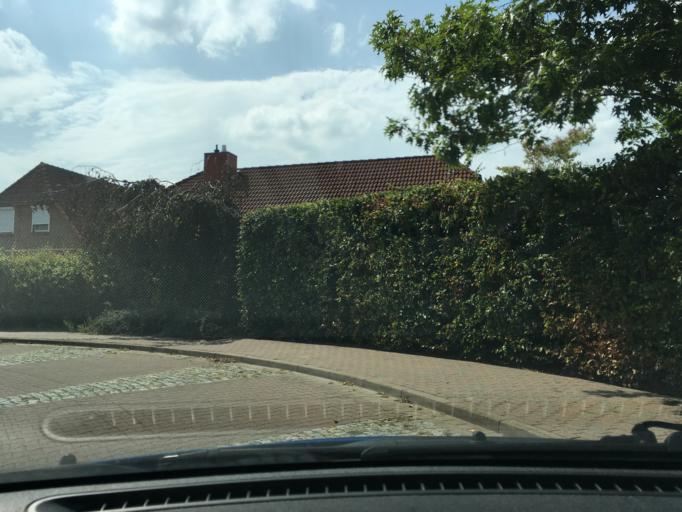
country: DE
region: Lower Saxony
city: Melbeck
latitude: 53.1784
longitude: 10.4149
